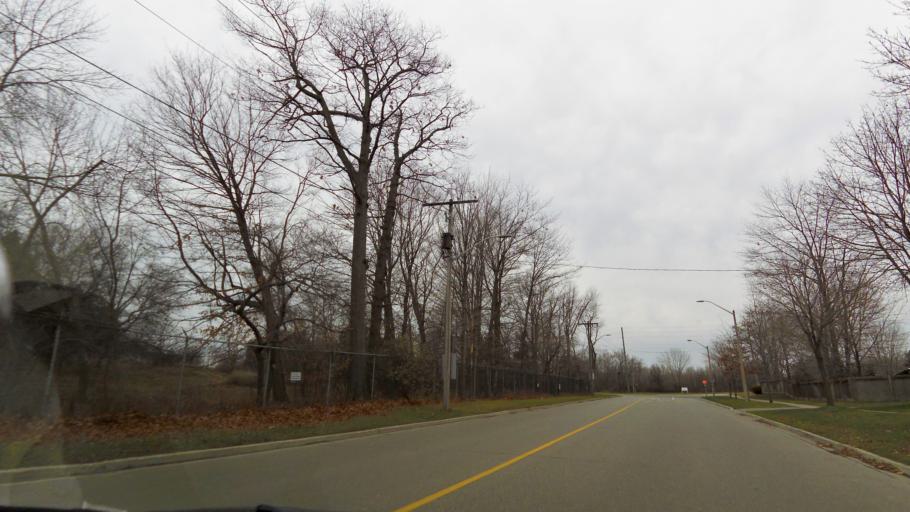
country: CA
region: Ontario
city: Mississauga
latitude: 43.5062
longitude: -79.6216
